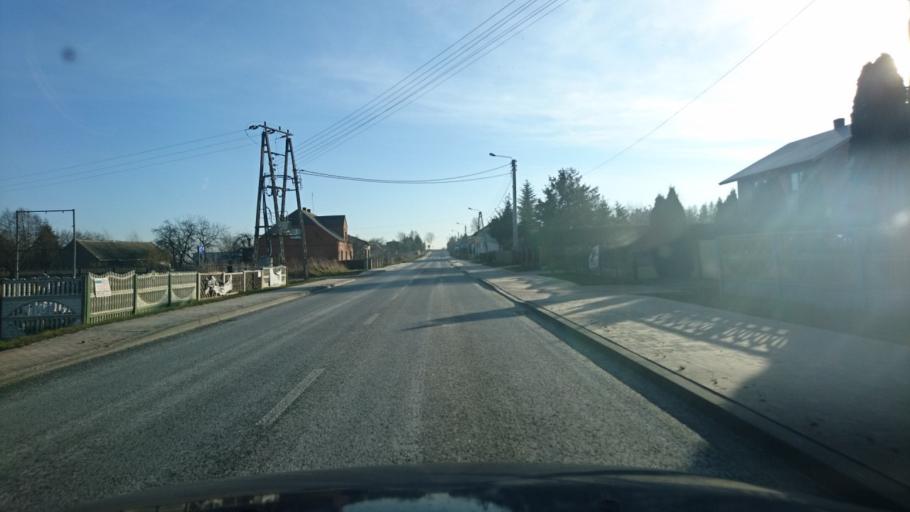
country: PL
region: Silesian Voivodeship
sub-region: Powiat klobucki
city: Starokrzepice
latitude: 51.0237
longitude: 18.6490
